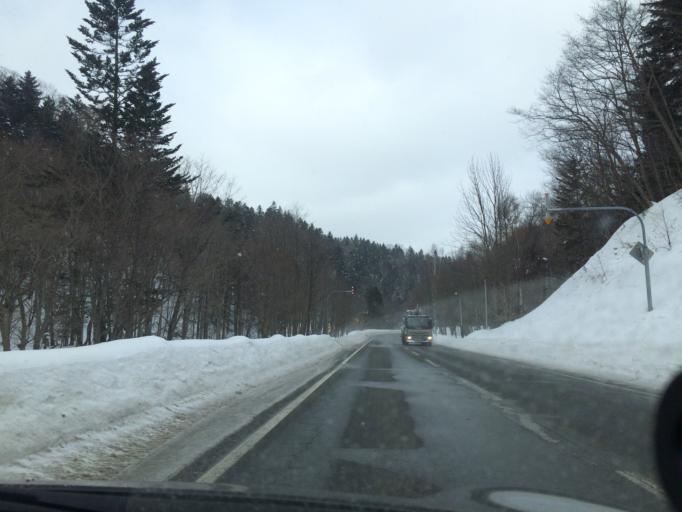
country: JP
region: Hokkaido
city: Shimo-furano
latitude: 43.0665
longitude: 142.6697
